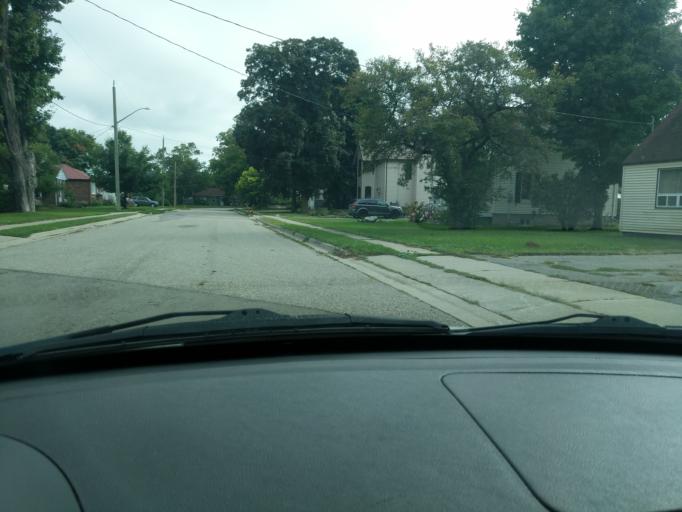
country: CA
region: Ontario
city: Cambridge
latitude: 43.4254
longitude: -80.3207
